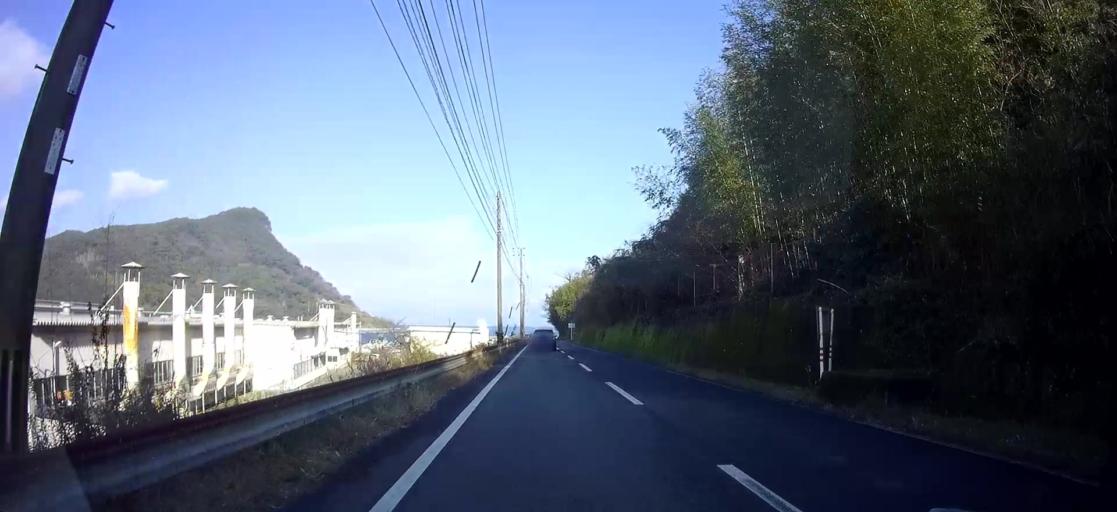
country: JP
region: Kumamoto
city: Minamata
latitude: 32.4168
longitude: 130.4052
